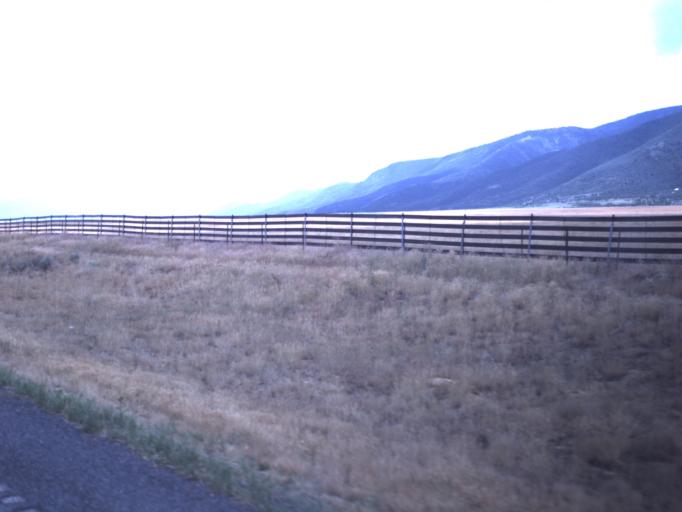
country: US
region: Utah
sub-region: Sanpete County
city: Fountain Green
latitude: 39.6710
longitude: -111.6635
